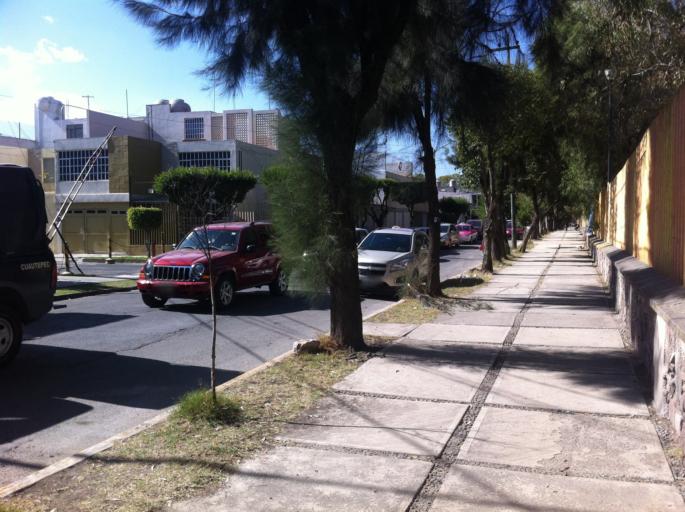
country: MX
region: Mexico
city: Colonia Lindavista
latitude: 19.4917
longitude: -99.1282
